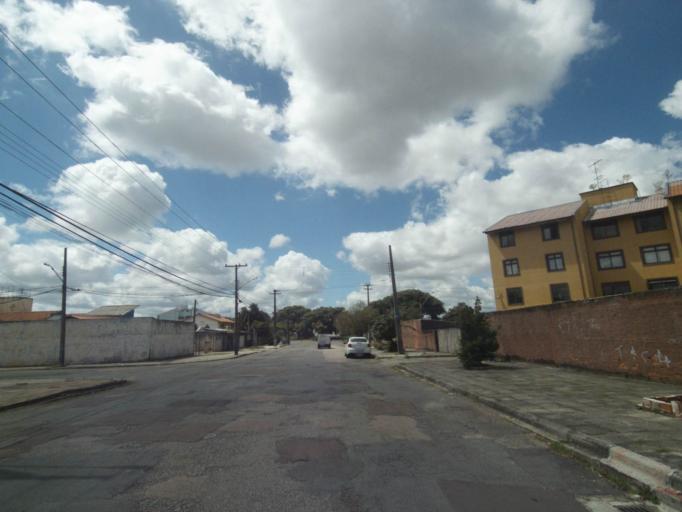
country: BR
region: Parana
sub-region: Pinhais
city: Pinhais
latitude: -25.4426
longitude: -49.2074
